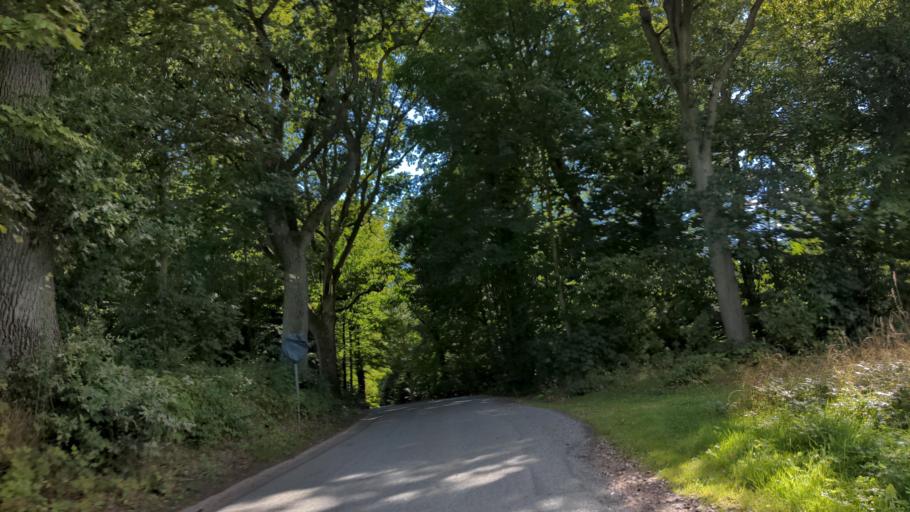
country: DE
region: Schleswig-Holstein
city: Kasseedorf
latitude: 54.1544
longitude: 10.7229
